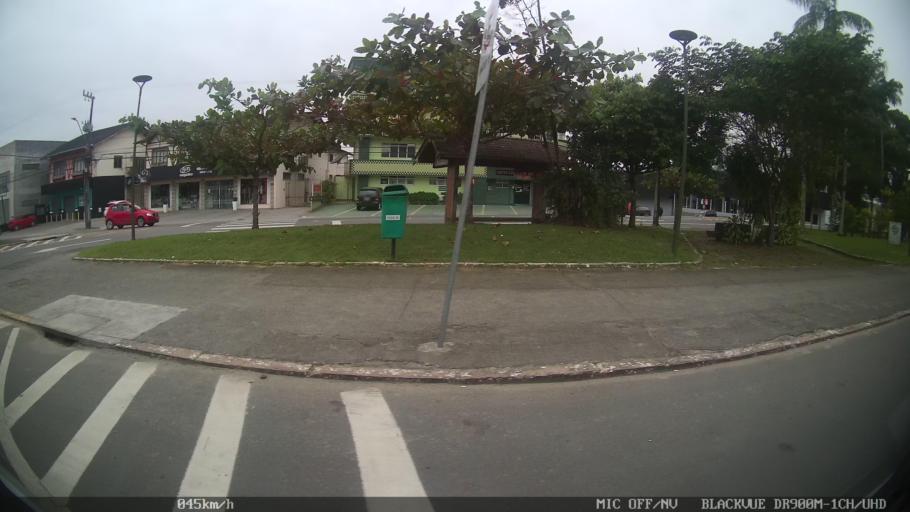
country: BR
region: Santa Catarina
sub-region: Joinville
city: Joinville
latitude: -26.3245
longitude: -48.8447
